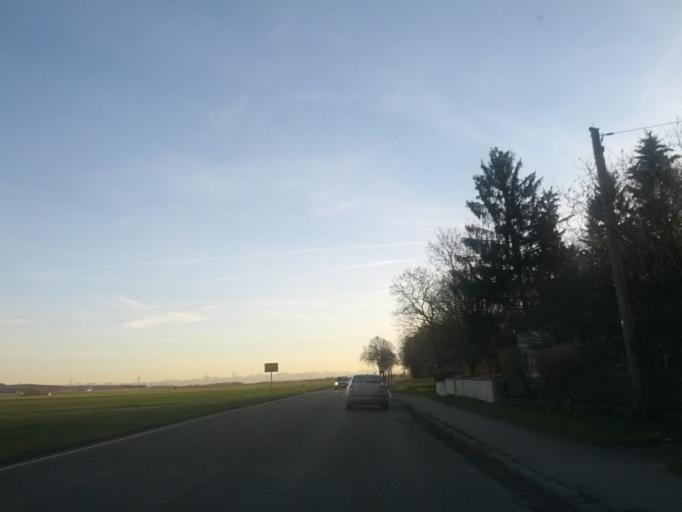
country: DE
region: Bavaria
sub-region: Swabia
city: Fellheim
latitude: 48.0671
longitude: 10.1526
